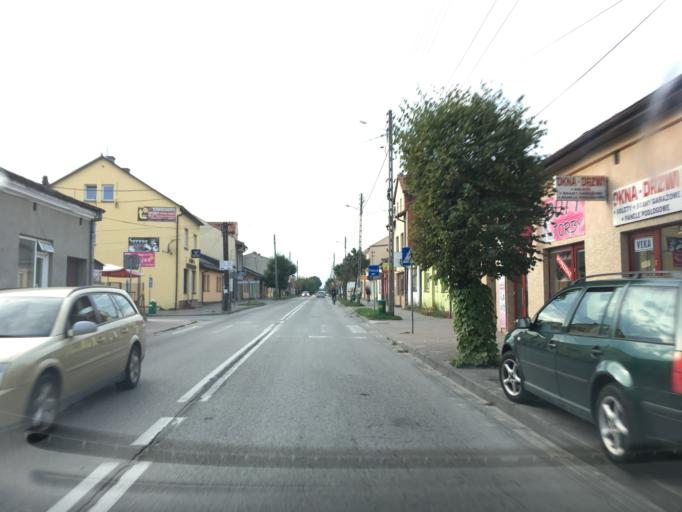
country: PL
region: Swietokrzyskie
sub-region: Powiat wloszczowski
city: Wloszczowa
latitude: 50.8530
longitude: 19.9654
